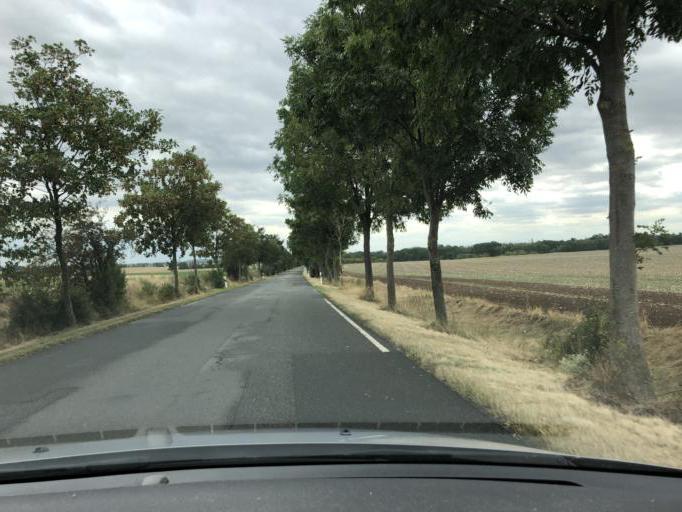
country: DE
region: Saxony-Anhalt
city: Brumby
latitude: 51.8683
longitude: 11.7118
